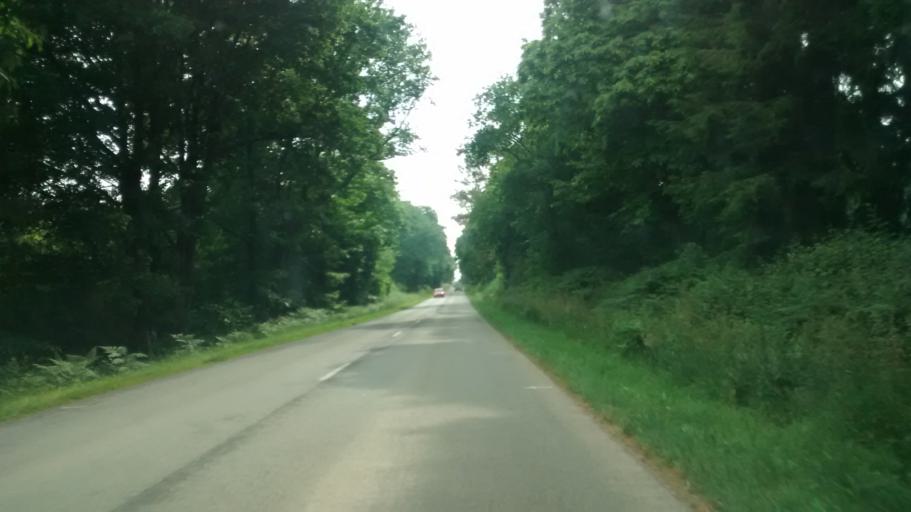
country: FR
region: Brittany
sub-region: Departement du Morbihan
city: Guer
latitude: 47.8869
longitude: -2.1758
